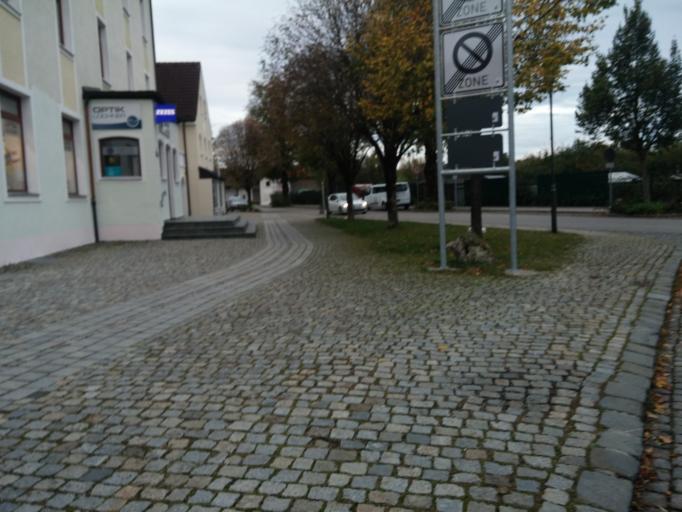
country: DE
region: Bavaria
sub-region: Upper Bavaria
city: Kirchseeon
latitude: 48.0702
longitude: 11.8900
